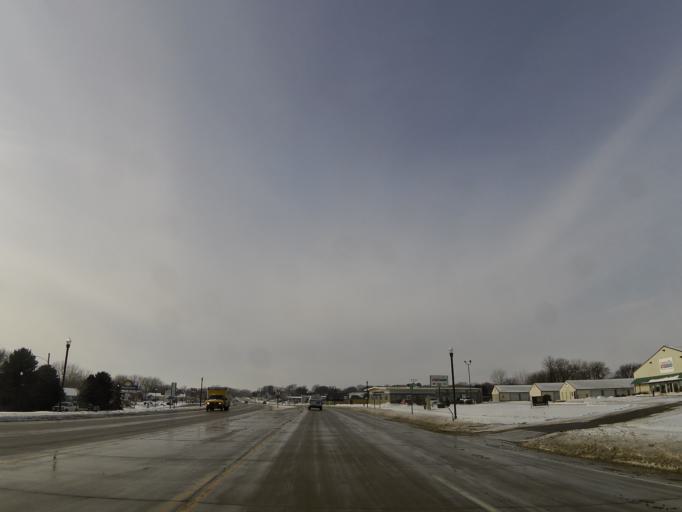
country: US
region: Minnesota
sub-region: McLeod County
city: Hutchinson
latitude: 44.8957
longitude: -94.3868
